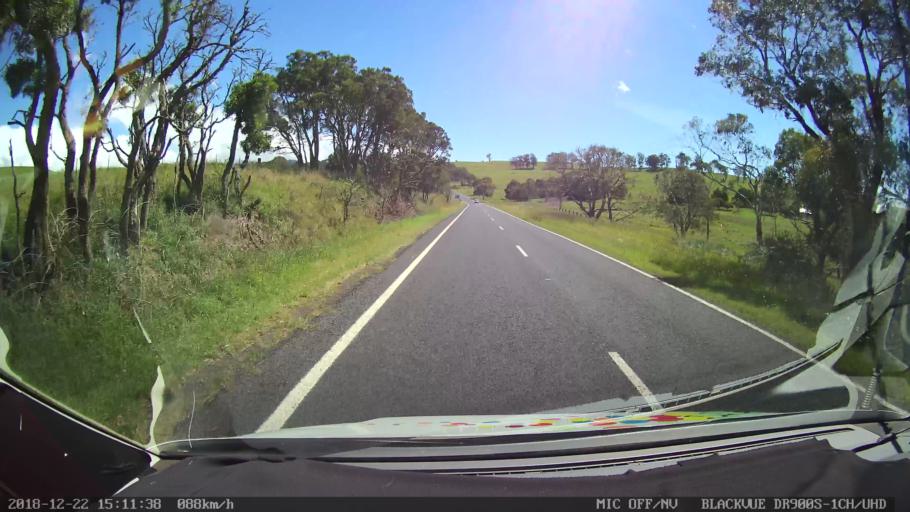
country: AU
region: New South Wales
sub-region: Bellingen
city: Dorrigo
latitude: -30.3460
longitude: 152.4008
